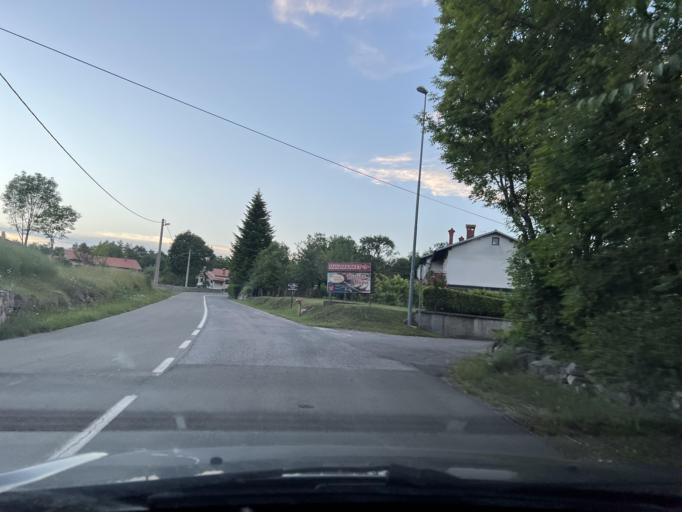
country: HR
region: Primorsko-Goranska
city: Klana
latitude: 45.4782
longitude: 14.2819
